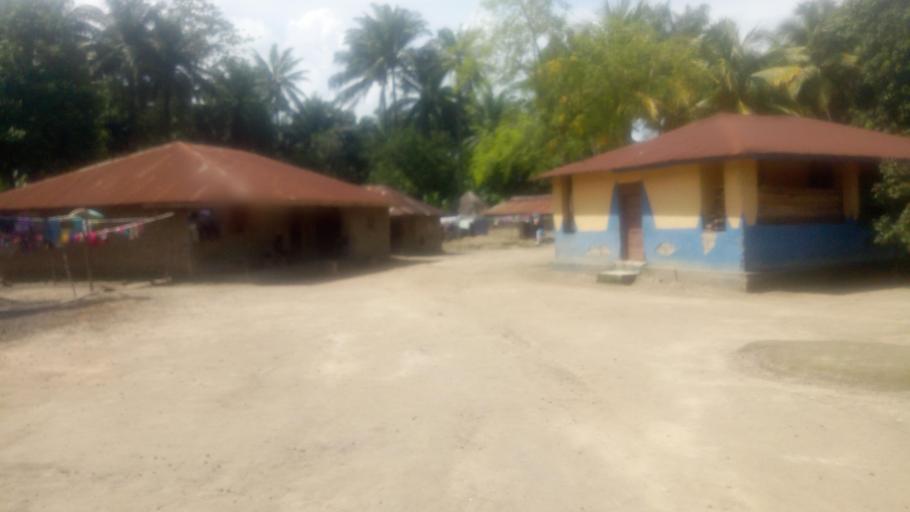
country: SL
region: Northern Province
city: Magburaka
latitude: 8.6631
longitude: -12.0700
